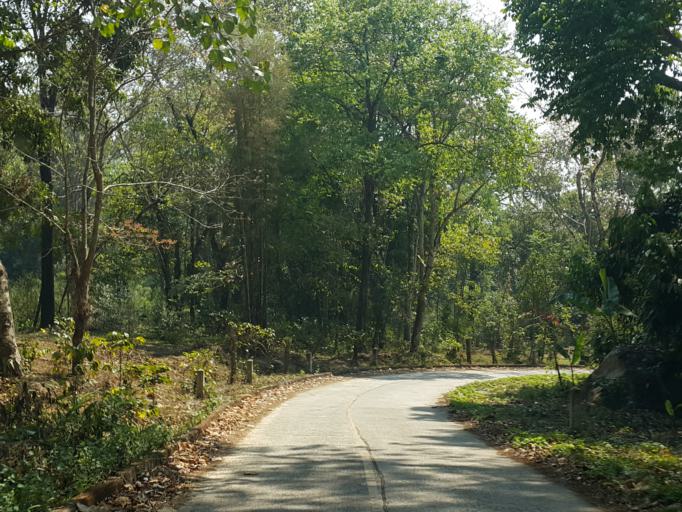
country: TH
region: Chiang Mai
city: Mae On
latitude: 18.8353
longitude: 99.3752
